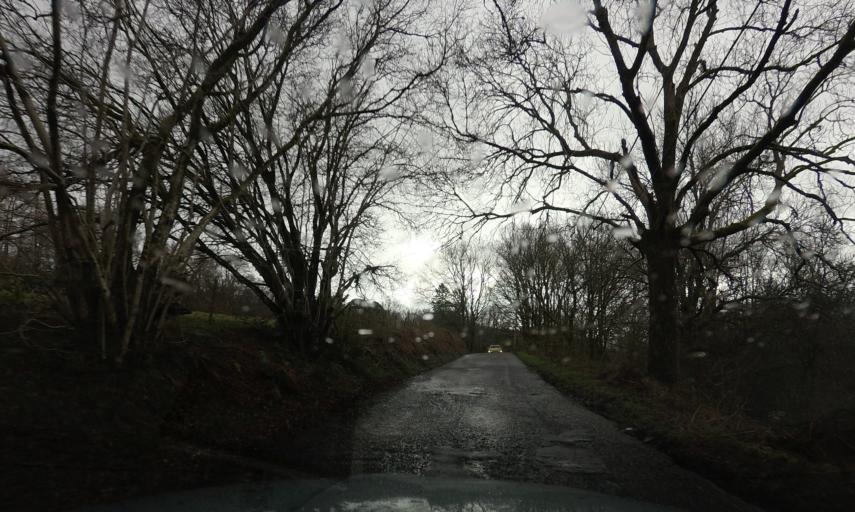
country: GB
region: Scotland
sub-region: West Dunbartonshire
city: Balloch
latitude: 56.1372
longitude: -4.6148
